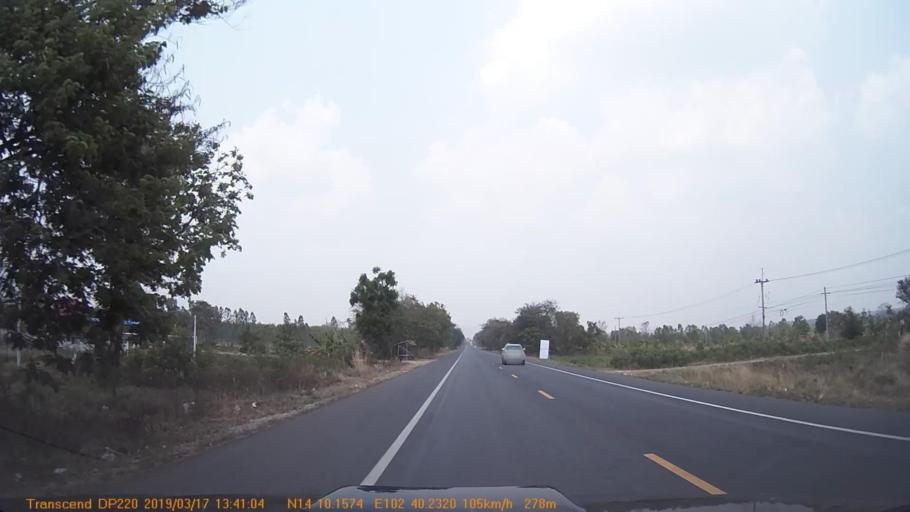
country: TH
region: Buriram
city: Non Din Daeng
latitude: 14.1695
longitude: 102.6707
